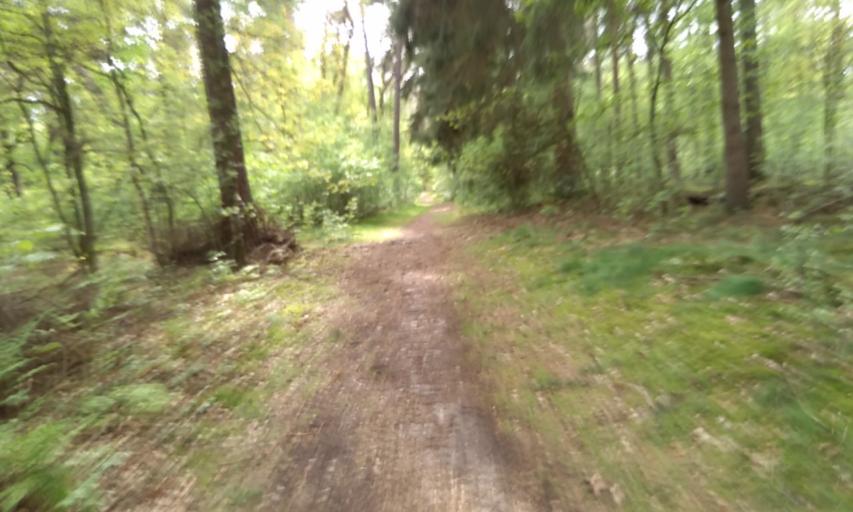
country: DE
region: Lower Saxony
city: Buxtehude
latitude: 53.4508
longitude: 9.6803
